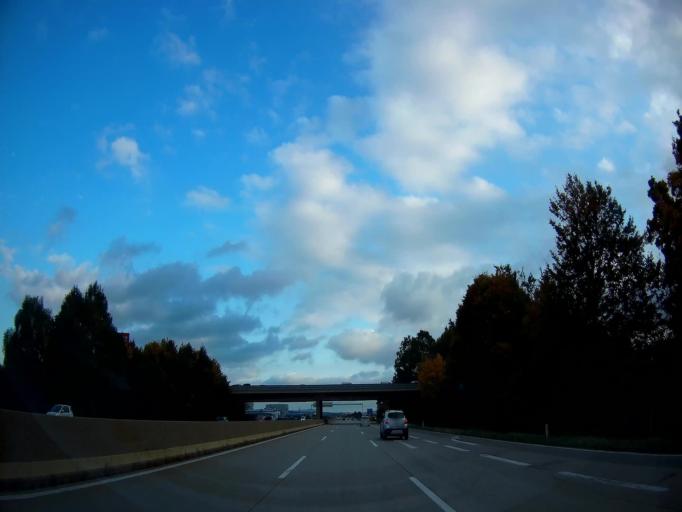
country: AT
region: Styria
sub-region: Politischer Bezirk Graz-Umgebung
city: Lieboch
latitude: 46.9610
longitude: 15.3478
